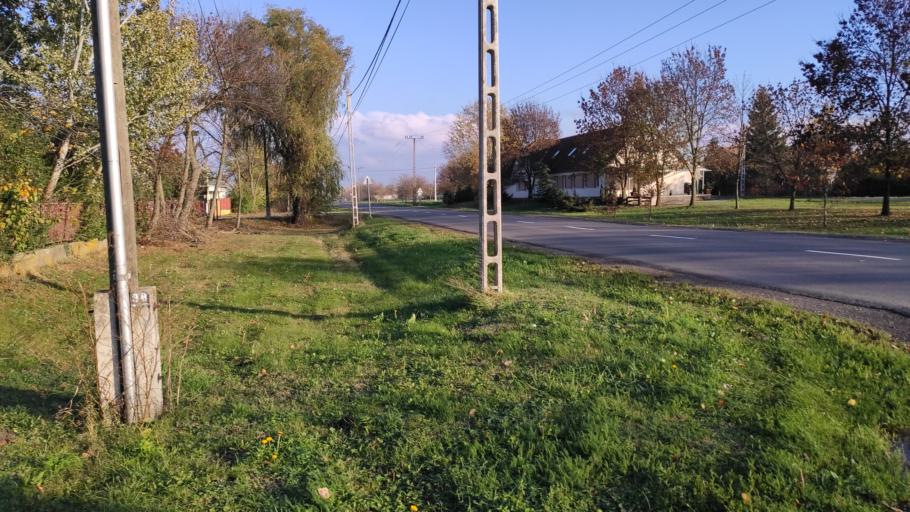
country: HU
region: Bekes
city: Mezobereny
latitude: 46.7612
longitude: 21.0449
